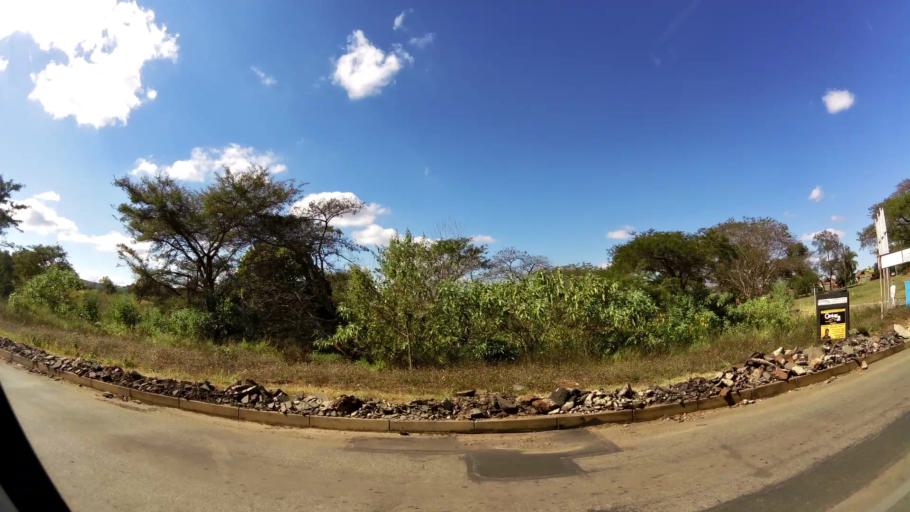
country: ZA
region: Limpopo
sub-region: Mopani District Municipality
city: Tzaneen
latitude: -23.8165
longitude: 30.1587
